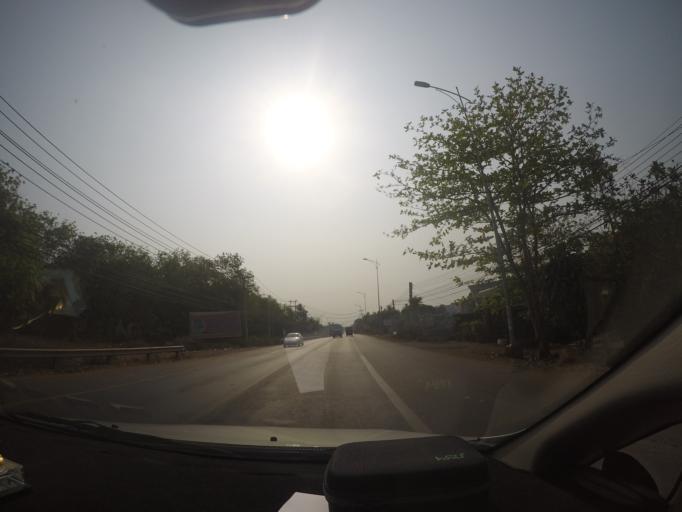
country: VN
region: Dong Nai
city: Vinh An
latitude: 11.0899
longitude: 107.1771
